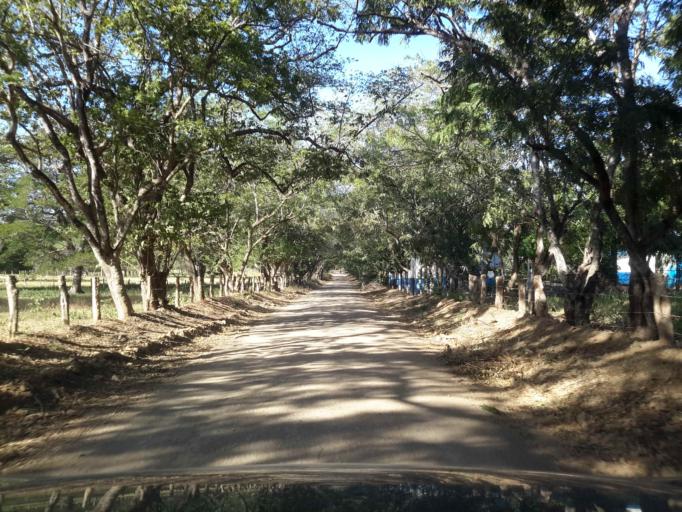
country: NI
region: Rivas
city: San Juan del Sur
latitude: 11.1987
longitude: -85.8049
